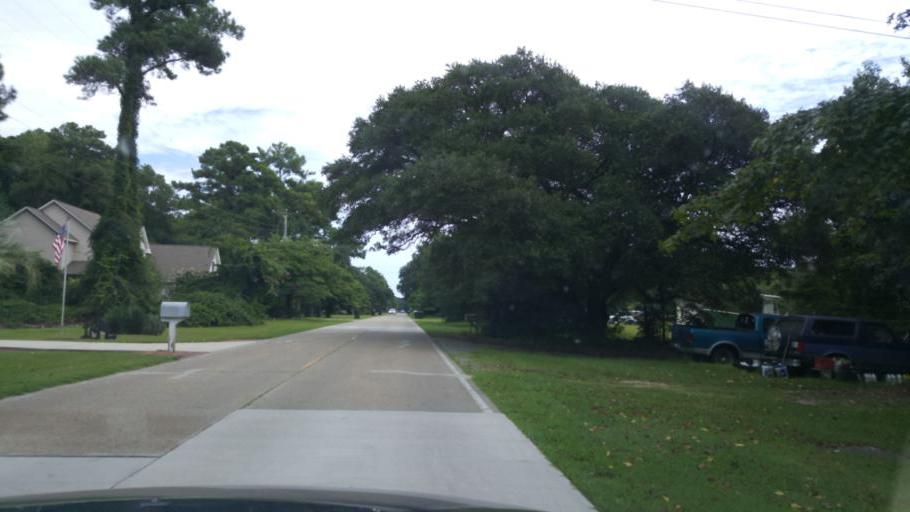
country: US
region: North Carolina
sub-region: Dare County
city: Manteo
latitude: 35.9268
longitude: -75.6996
